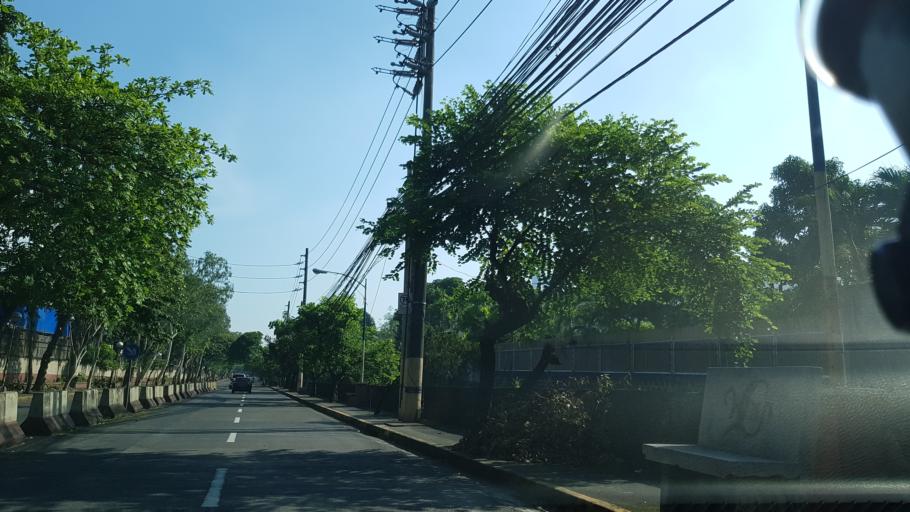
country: PH
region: Metro Manila
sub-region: Pasig
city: Pasig City
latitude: 14.5889
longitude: 121.0712
